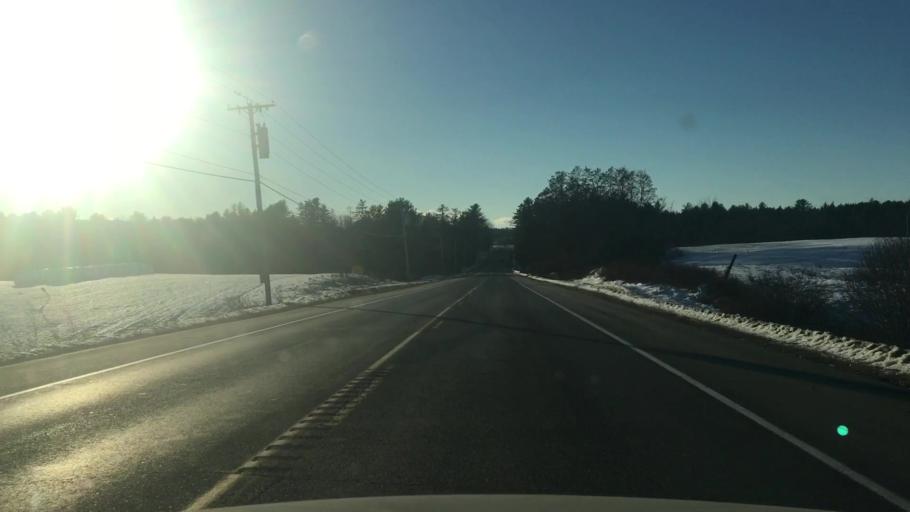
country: US
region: Maine
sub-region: Somerset County
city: Norridgewock
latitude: 44.7018
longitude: -69.8311
